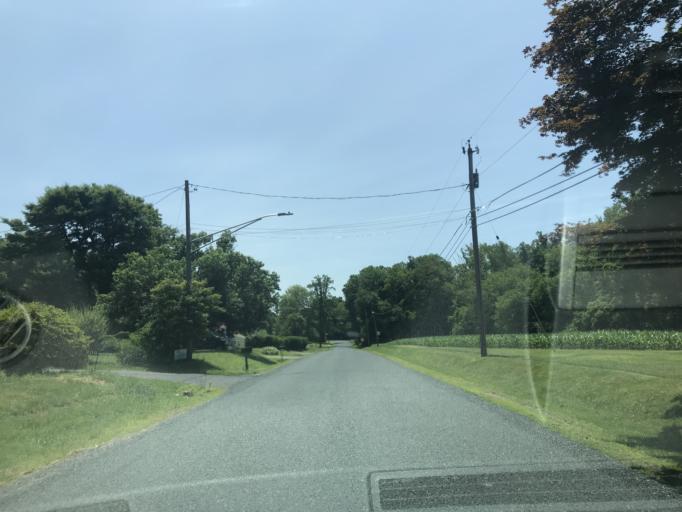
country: US
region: Maryland
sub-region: Harford County
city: Bel Air South
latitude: 39.5490
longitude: -76.2678
